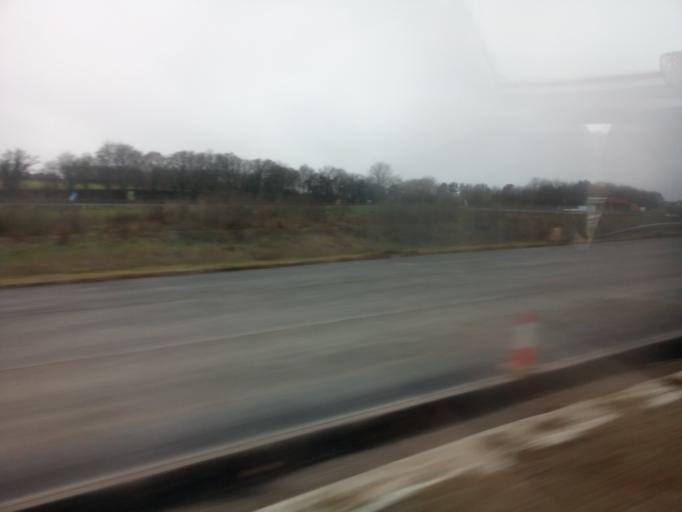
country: GB
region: England
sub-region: Cornwall
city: Liskeard
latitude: 50.4583
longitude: -4.5062
